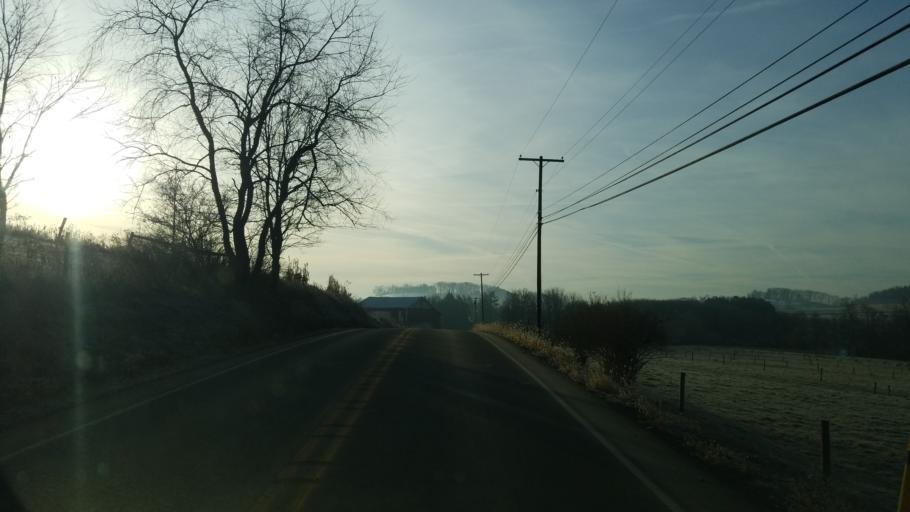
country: US
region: Pennsylvania
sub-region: Indiana County
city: Chevy Chase Heights
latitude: 40.8685
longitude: -79.2366
